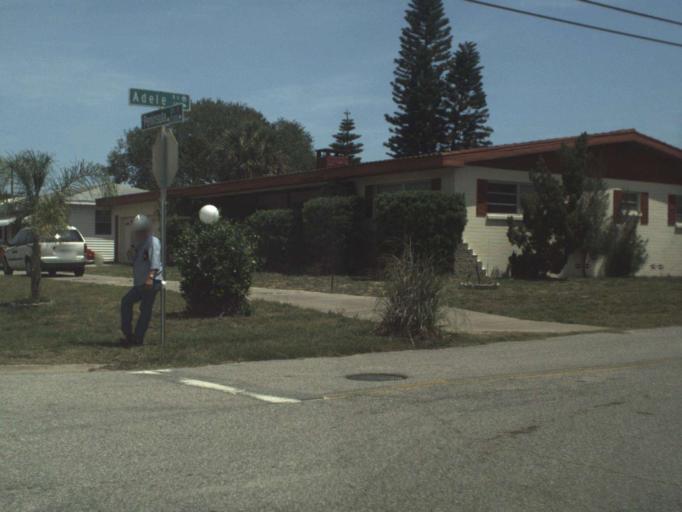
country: US
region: Florida
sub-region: Volusia County
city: Daytona Beach Shores
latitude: 29.1975
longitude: -80.9976
